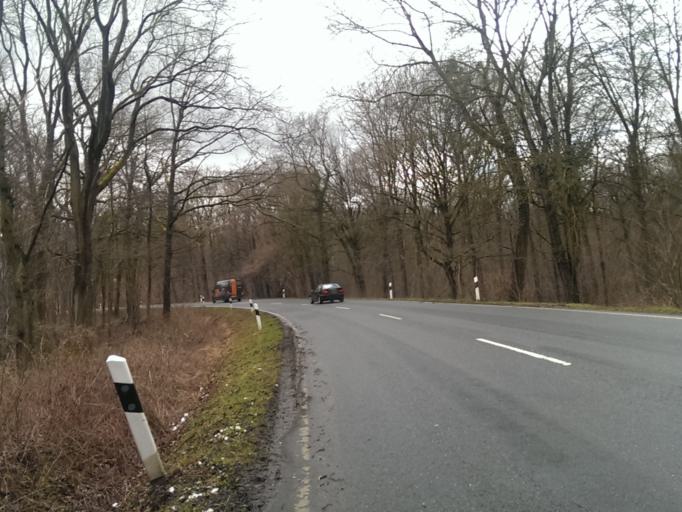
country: DE
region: Lower Saxony
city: Schellerten
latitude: 52.1302
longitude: 10.0547
